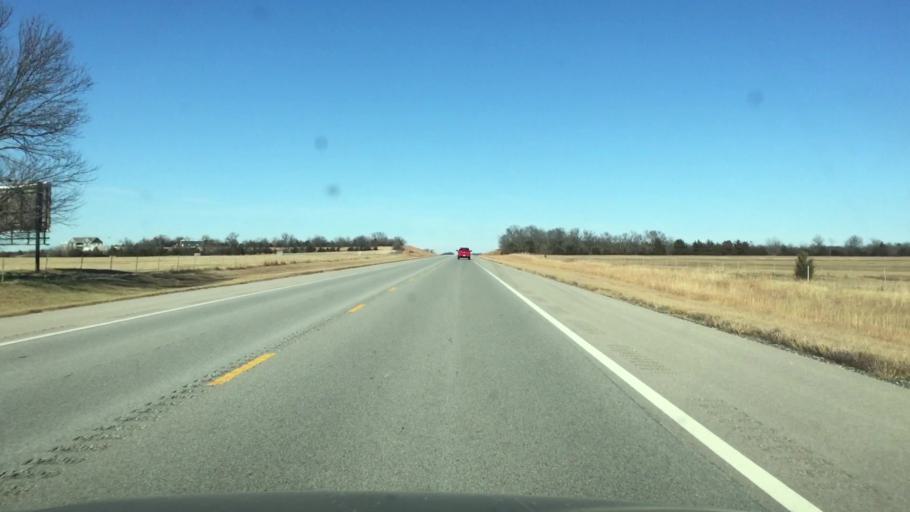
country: US
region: Kansas
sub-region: Allen County
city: Iola
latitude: 37.9671
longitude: -95.3815
